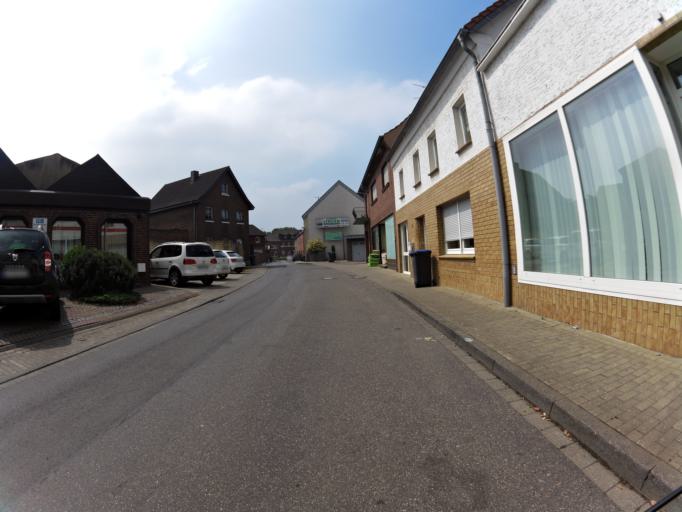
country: DE
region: North Rhine-Westphalia
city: Huckelhoven
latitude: 51.0401
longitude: 6.2192
